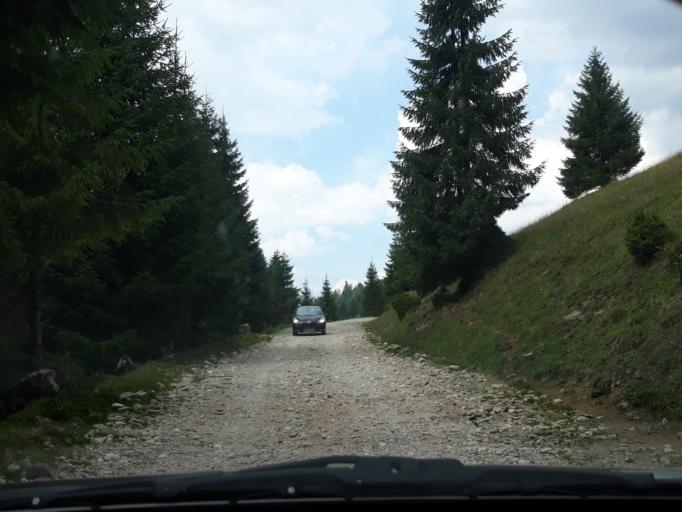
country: RO
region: Alba
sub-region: Comuna Arieseni
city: Arieseni
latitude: 46.5843
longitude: 22.6982
